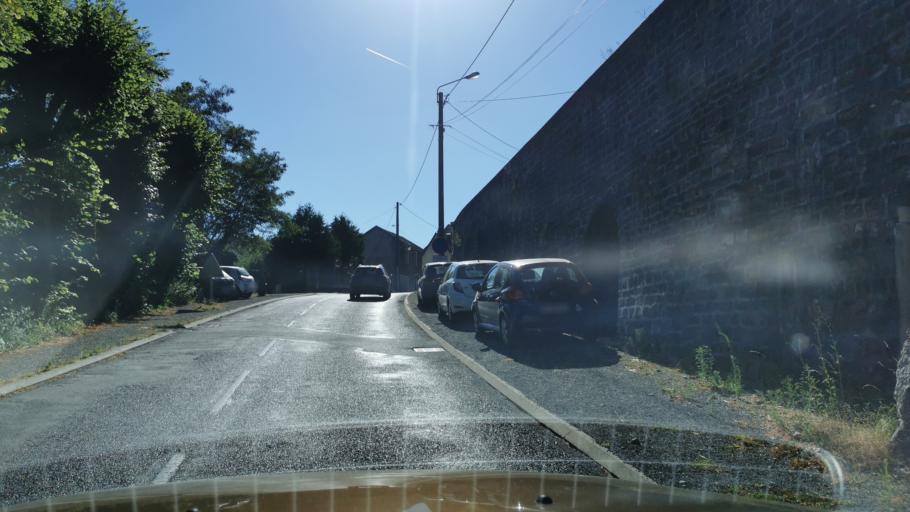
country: FR
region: Bourgogne
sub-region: Departement de Saone-et-Loire
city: Montcenis
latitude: 46.7883
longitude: 4.3933
